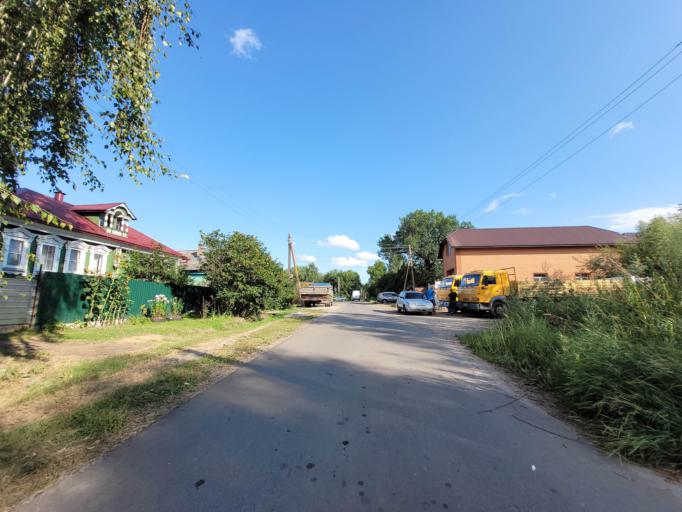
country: RU
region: Moskovskaya
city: Konobeyevo
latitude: 55.4115
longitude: 38.6967
